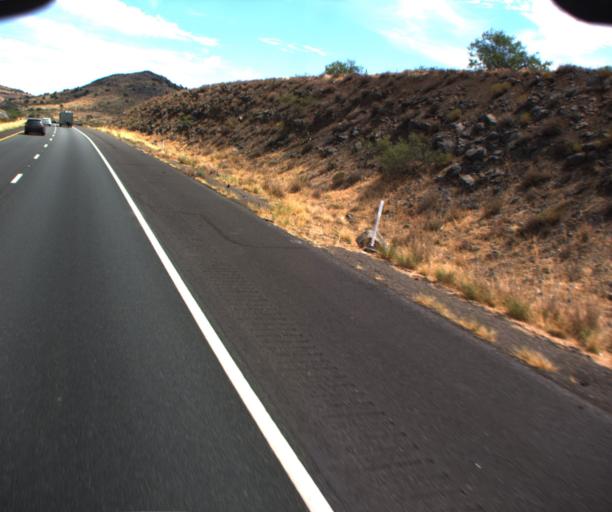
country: US
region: Arizona
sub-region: Yavapai County
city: Cordes Lakes
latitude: 34.4655
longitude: -112.0259
